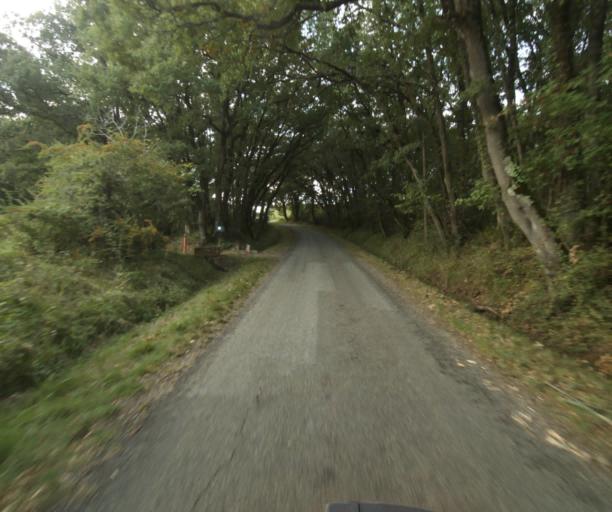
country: FR
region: Midi-Pyrenees
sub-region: Departement de la Haute-Garonne
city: Launac
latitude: 43.8116
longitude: 1.1078
